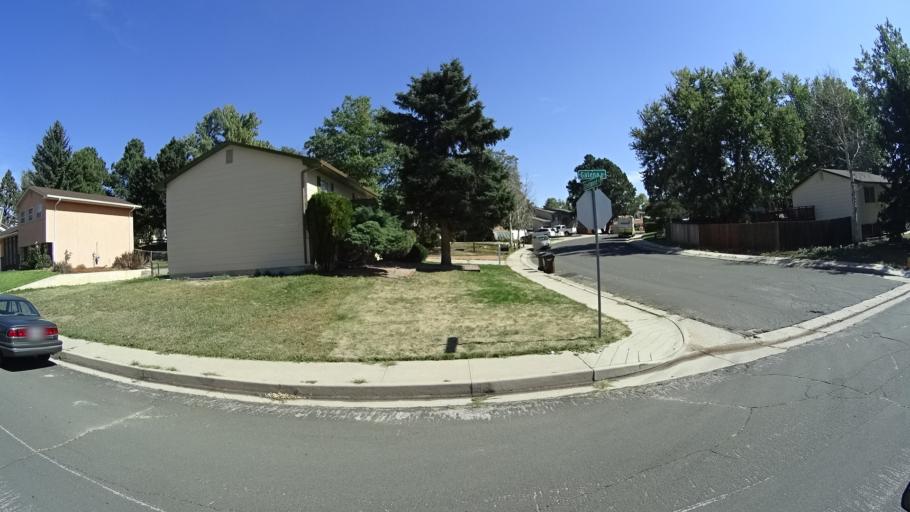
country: US
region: Colorado
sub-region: El Paso County
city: Cimarron Hills
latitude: 38.9059
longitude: -104.7674
